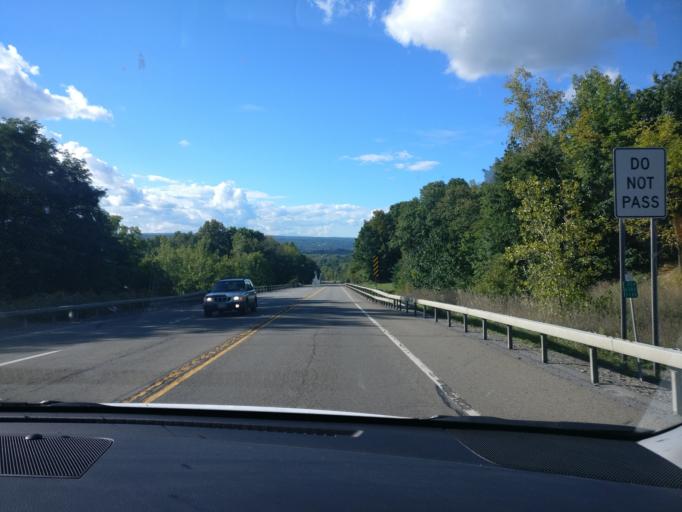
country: US
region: New York
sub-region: Schuyler County
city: Montour Falls
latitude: 42.3435
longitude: -76.8275
